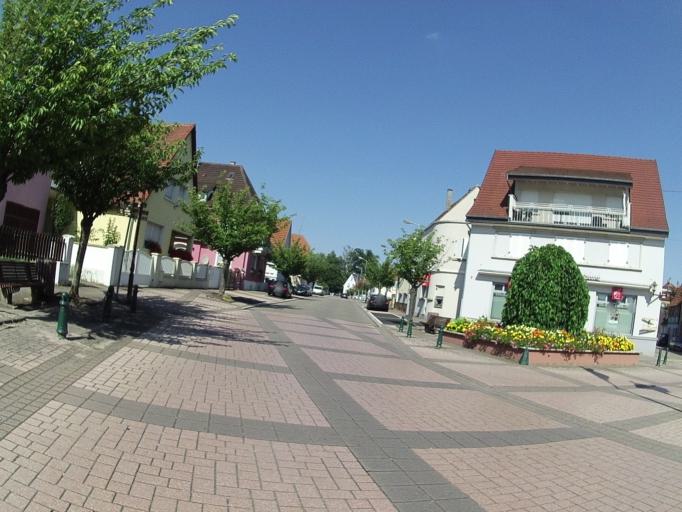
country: DE
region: Rheinland-Pfalz
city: Berg
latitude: 48.9752
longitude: 8.1808
